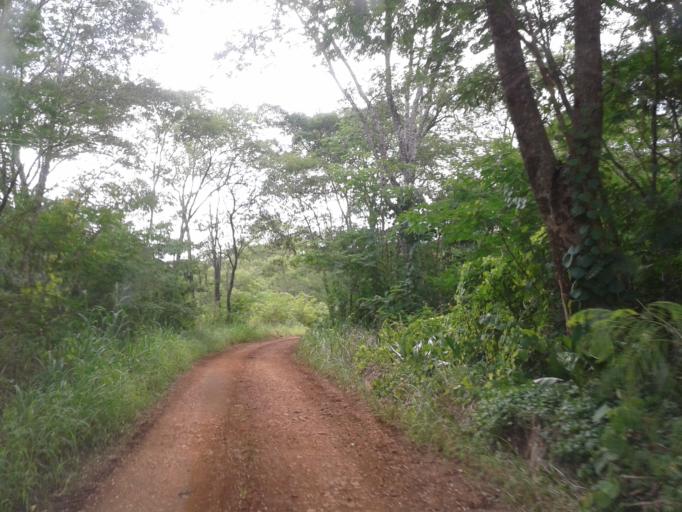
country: BR
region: Minas Gerais
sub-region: Centralina
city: Centralina
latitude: -18.6845
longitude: -49.2216
